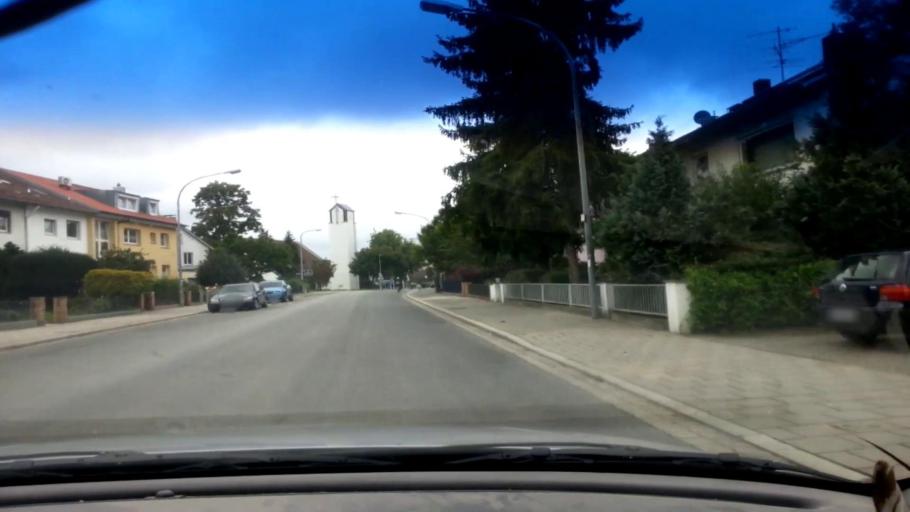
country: DE
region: Bavaria
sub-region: Upper Franconia
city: Bamberg
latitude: 49.8852
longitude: 10.9138
